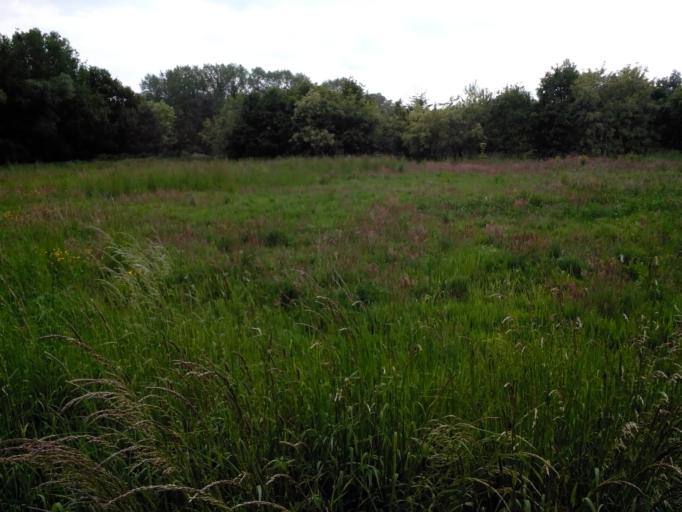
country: BE
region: Flanders
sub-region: Provincie Vlaams-Brabant
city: Rotselaar
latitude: 50.9716
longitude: 4.7238
